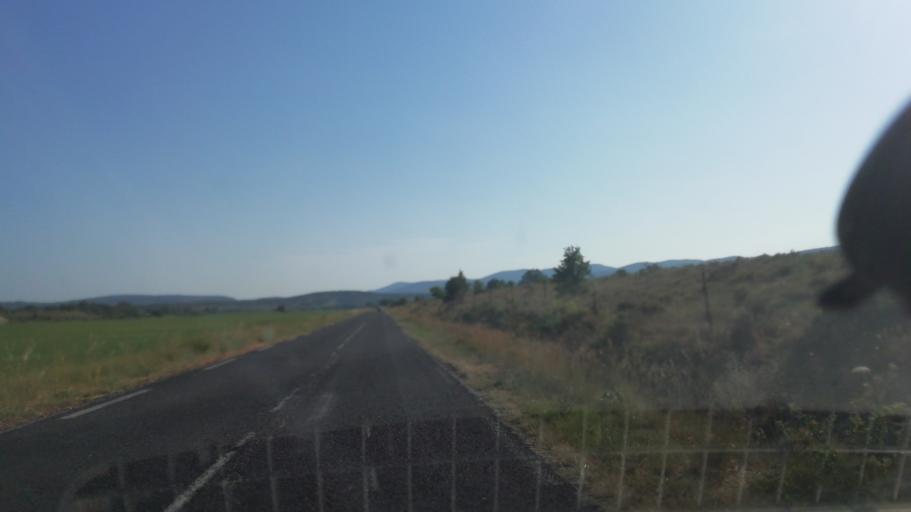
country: FR
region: Languedoc-Roussillon
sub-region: Departement de l'Herault
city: Saint-Martin-de-Londres
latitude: 43.8207
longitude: 3.7628
